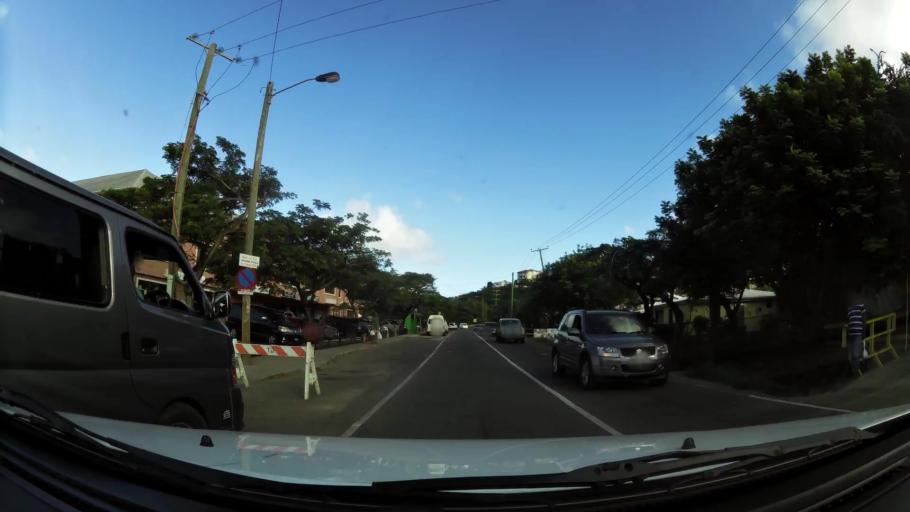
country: LC
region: Gros-Islet
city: Gros Islet
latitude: 14.0679
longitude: -60.9537
